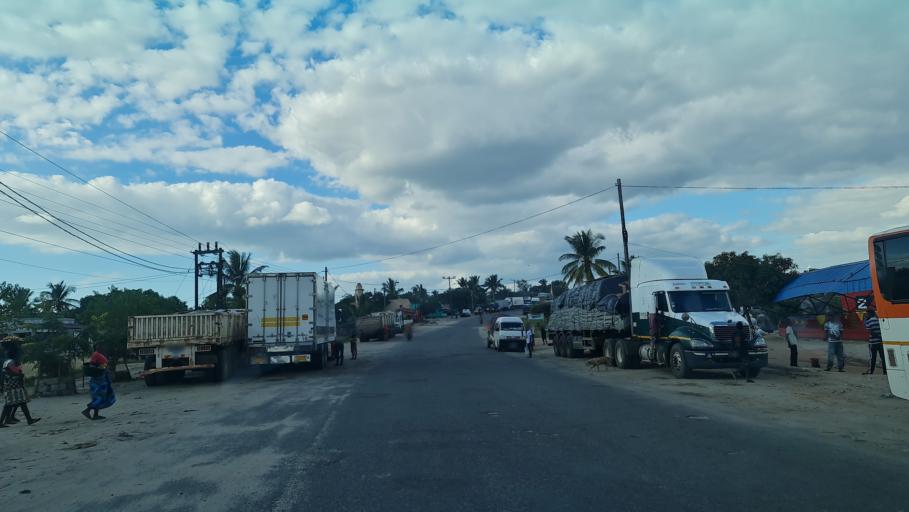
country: MZ
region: Manica
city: Chimoio
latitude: -19.2119
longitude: 33.9246
